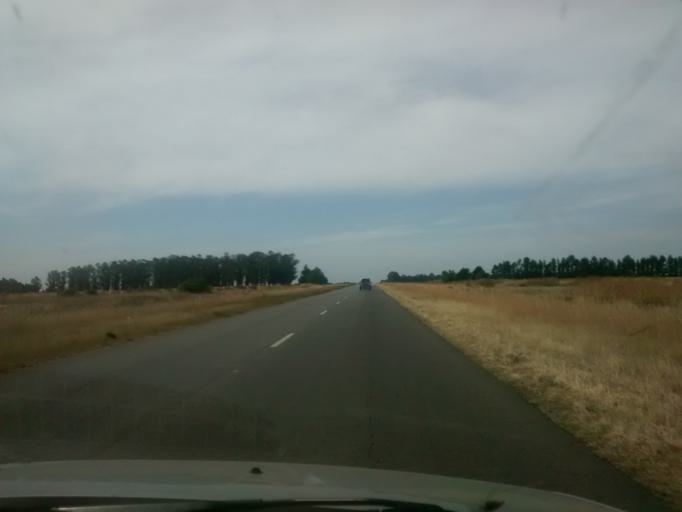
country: AR
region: Buenos Aires
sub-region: Partido de Loberia
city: Loberia
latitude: -38.1312
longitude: -58.7528
